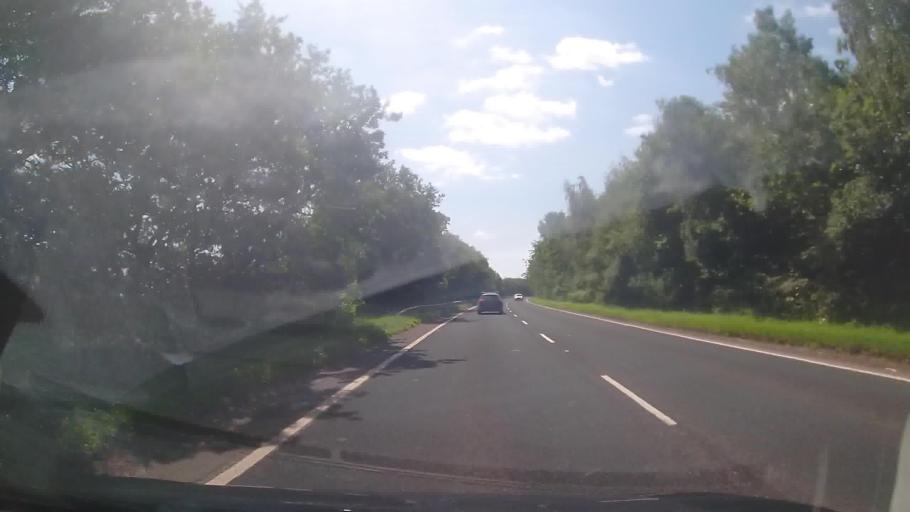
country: GB
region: England
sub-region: Shropshire
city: Ludlow
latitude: 52.3730
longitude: -2.6975
